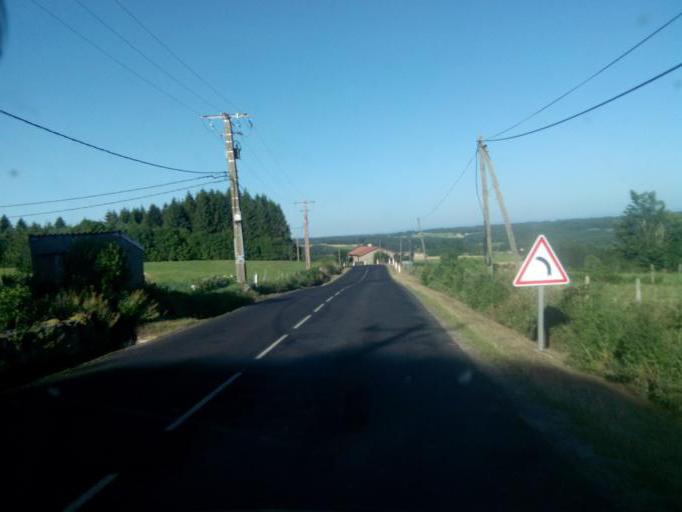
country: FR
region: Auvergne
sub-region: Departement de la Haute-Loire
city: Fontannes
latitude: 45.3032
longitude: 3.7708
